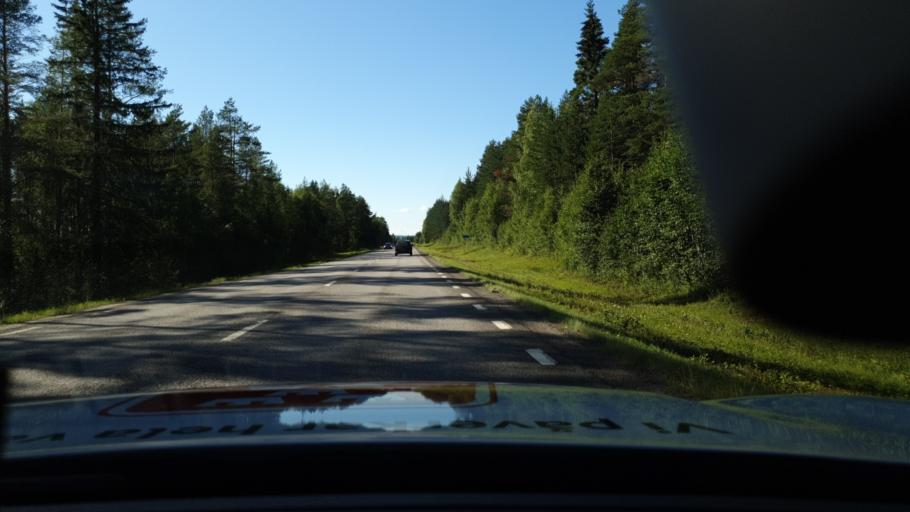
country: SE
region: Norrbotten
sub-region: Pitea Kommun
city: Rosvik
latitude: 65.5599
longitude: 21.7993
